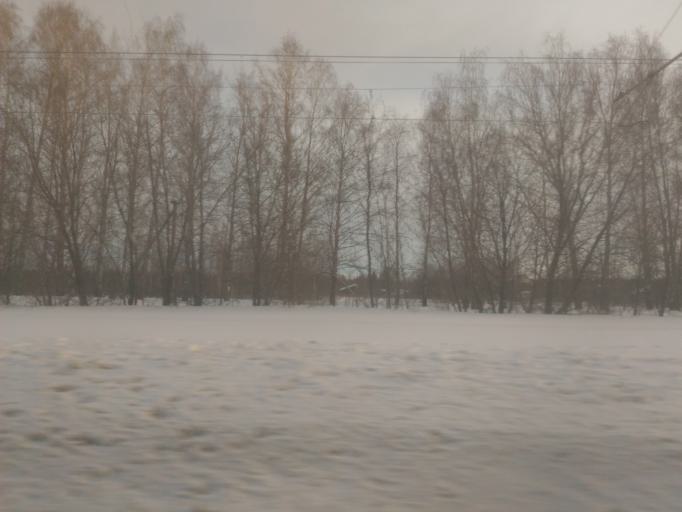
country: RU
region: Ulyanovsk
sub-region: Ulyanovskiy Rayon
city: Ulyanovsk
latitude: 54.3648
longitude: 48.3284
